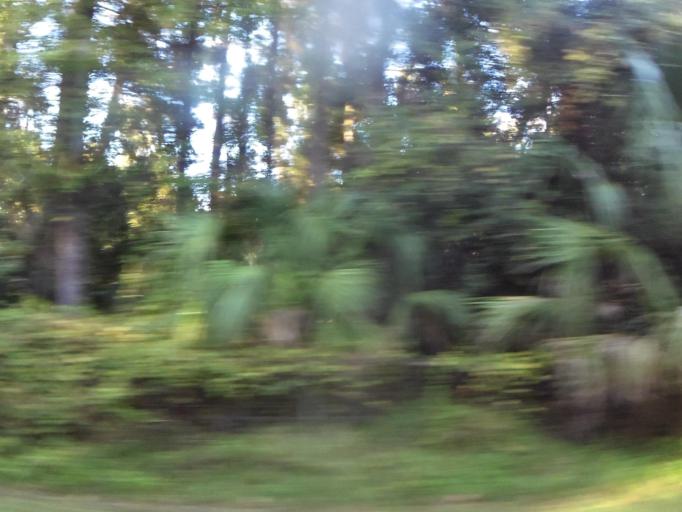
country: US
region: Florida
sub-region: Marion County
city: Citra
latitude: 29.4541
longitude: -82.0970
